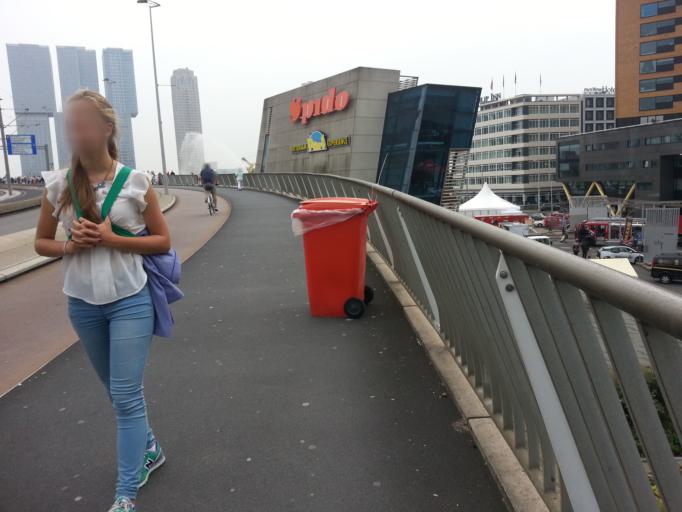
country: NL
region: South Holland
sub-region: Gemeente Rotterdam
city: Rotterdam
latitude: 51.9110
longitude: 4.4824
